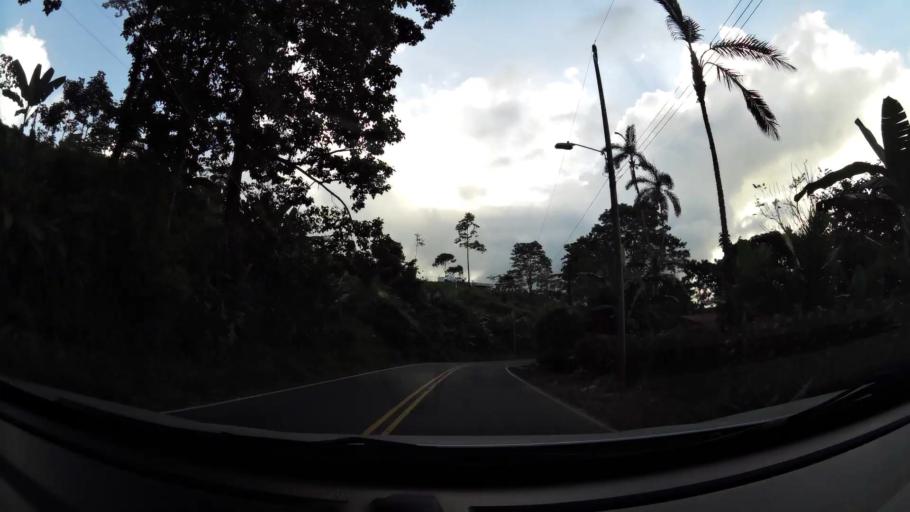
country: CR
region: Limon
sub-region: Canton de Siquirres
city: Siquirres
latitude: 10.0036
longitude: -83.5734
